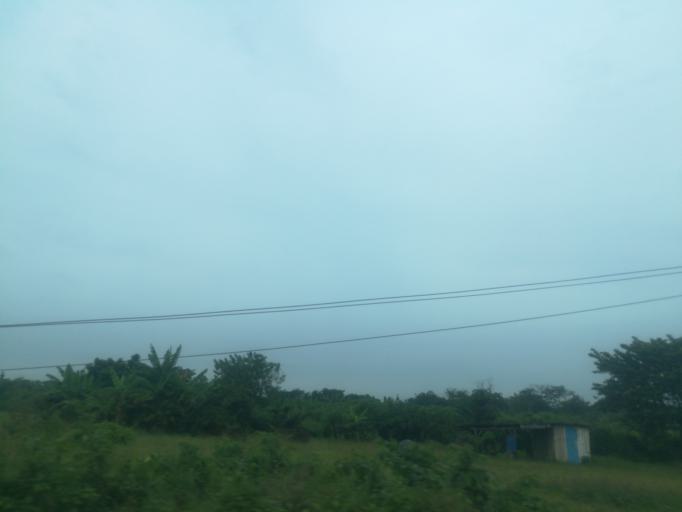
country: NG
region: Oyo
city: Egbeda
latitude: 7.3828
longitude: 4.0170
